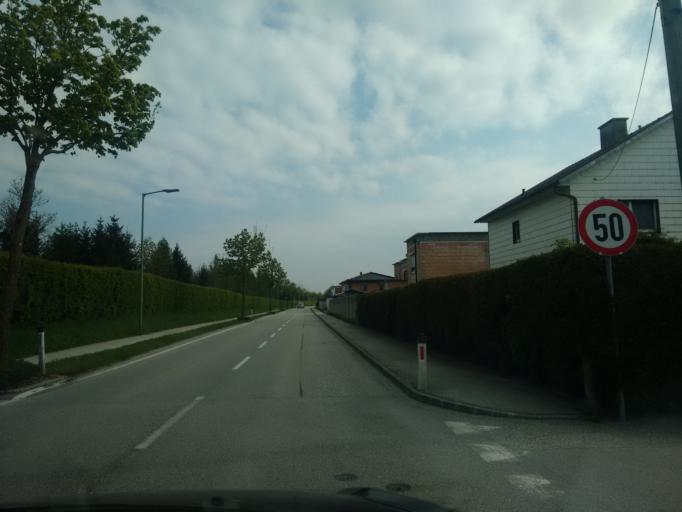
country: AT
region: Upper Austria
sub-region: Wels-Land
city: Gunskirchen
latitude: 48.1398
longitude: 13.9614
